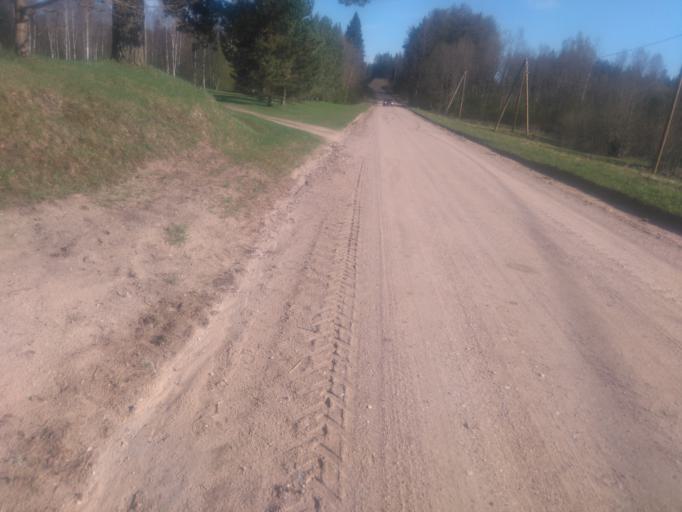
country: LV
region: Vecpiebalga
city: Vecpiebalga
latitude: 57.0160
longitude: 25.8354
